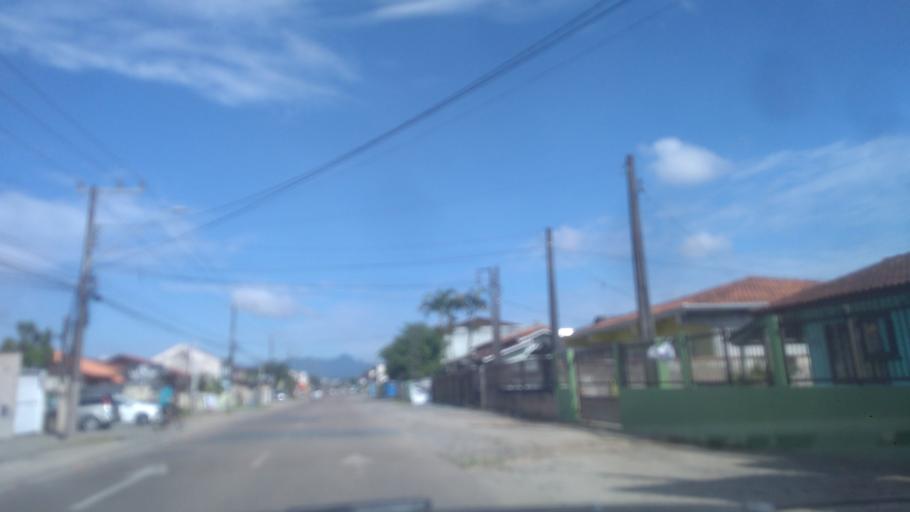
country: BR
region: Santa Catarina
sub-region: Joinville
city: Joinville
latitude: -26.3214
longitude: -48.8121
